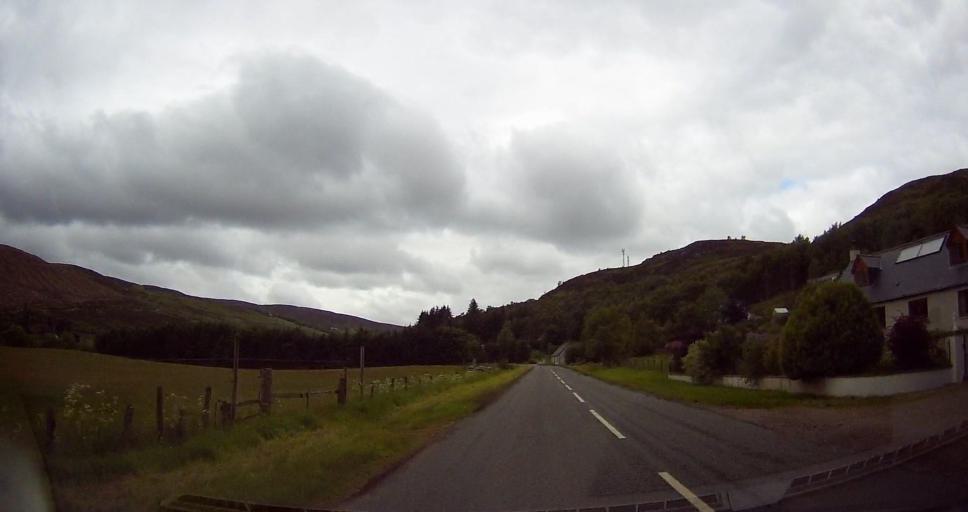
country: GB
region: Scotland
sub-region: Highland
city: Dornoch
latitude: 58.0051
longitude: -4.1801
